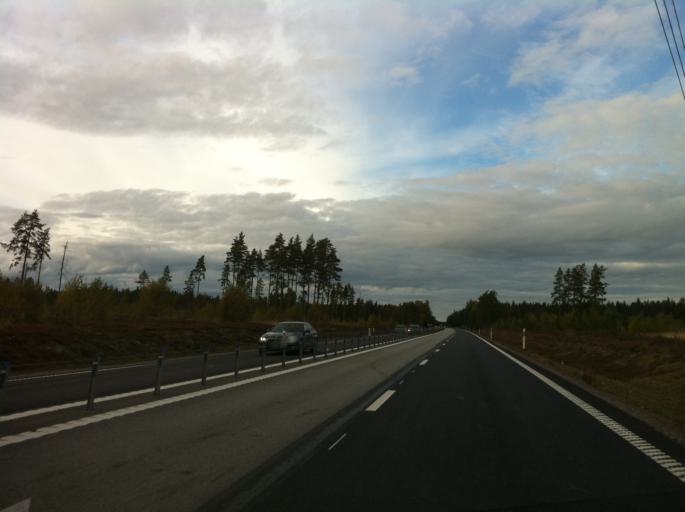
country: SE
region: OErebro
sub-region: Askersunds Kommun
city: Asbro
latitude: 58.9915
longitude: 15.0407
